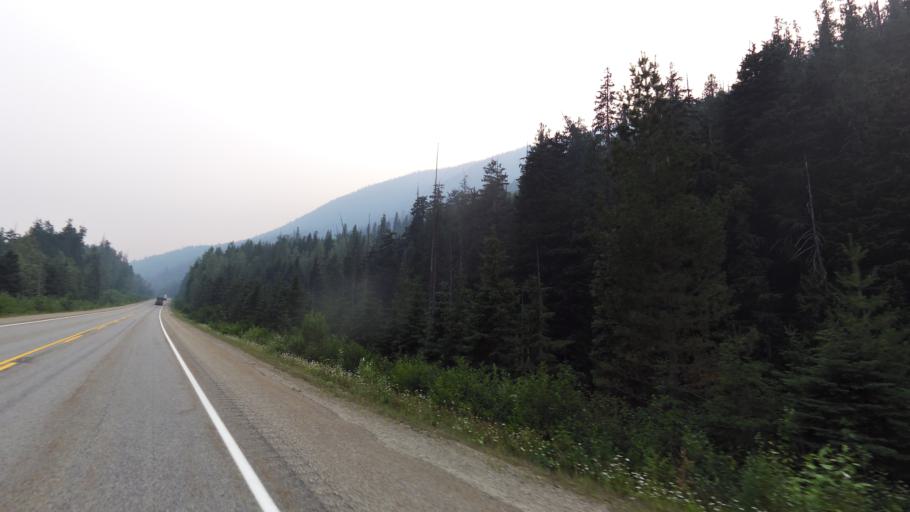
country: CA
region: Alberta
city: Jasper Park Lodge
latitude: 52.3144
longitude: -119.1790
